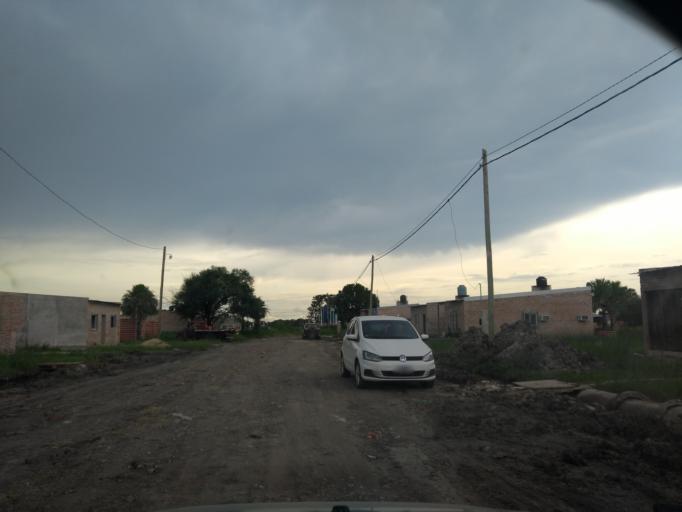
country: AR
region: Chaco
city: Resistencia
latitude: -27.4673
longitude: -59.0312
